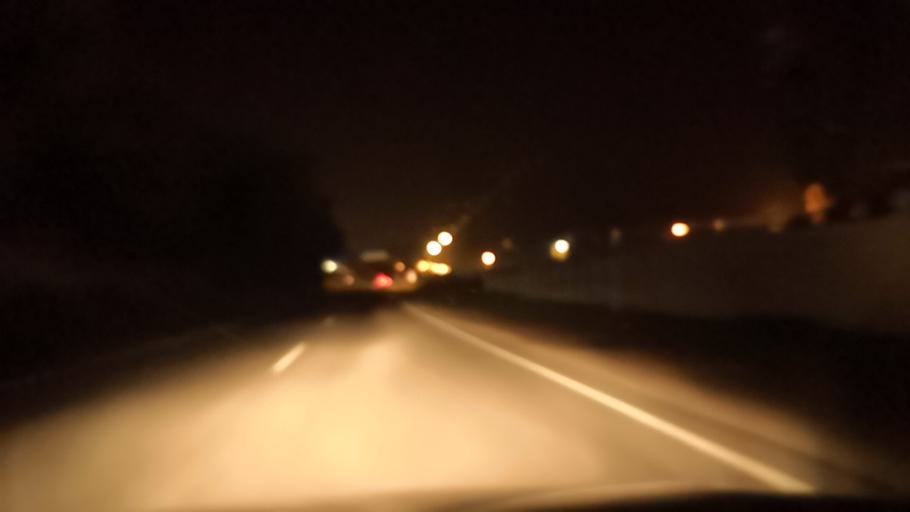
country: PT
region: Setubal
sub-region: Setubal
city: Setubal
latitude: 38.5100
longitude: -8.8529
